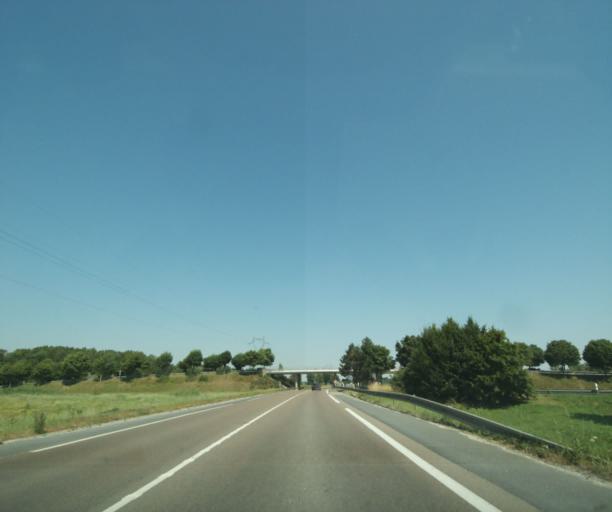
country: FR
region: Champagne-Ardenne
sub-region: Departement de la Marne
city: Frignicourt
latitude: 48.7129
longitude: 4.6382
